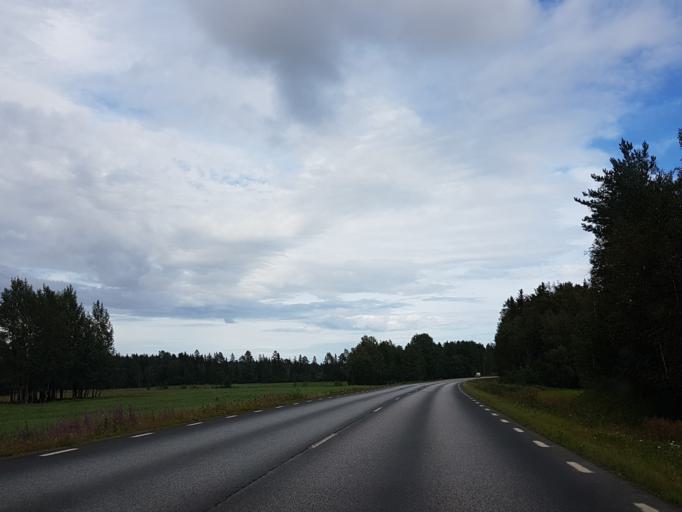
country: SE
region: Vaesterbotten
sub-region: Umea Kommun
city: Taftea
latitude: 63.8155
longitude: 20.4071
